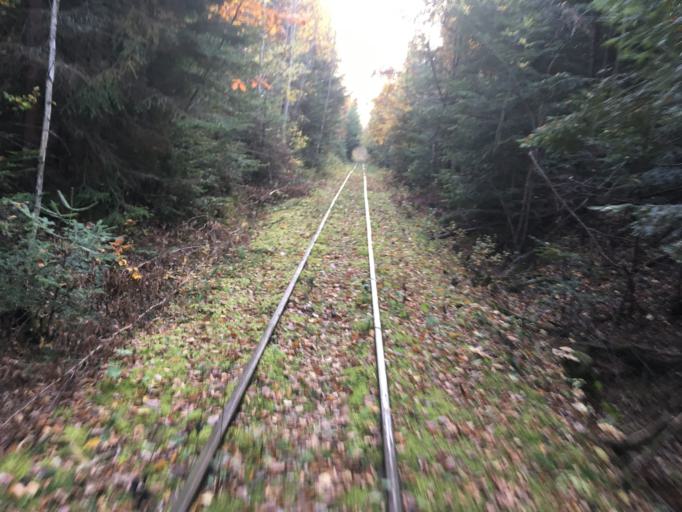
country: PL
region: Swietokrzyskie
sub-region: Powiat starachowicki
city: Starachowice
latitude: 51.0743
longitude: 21.1495
